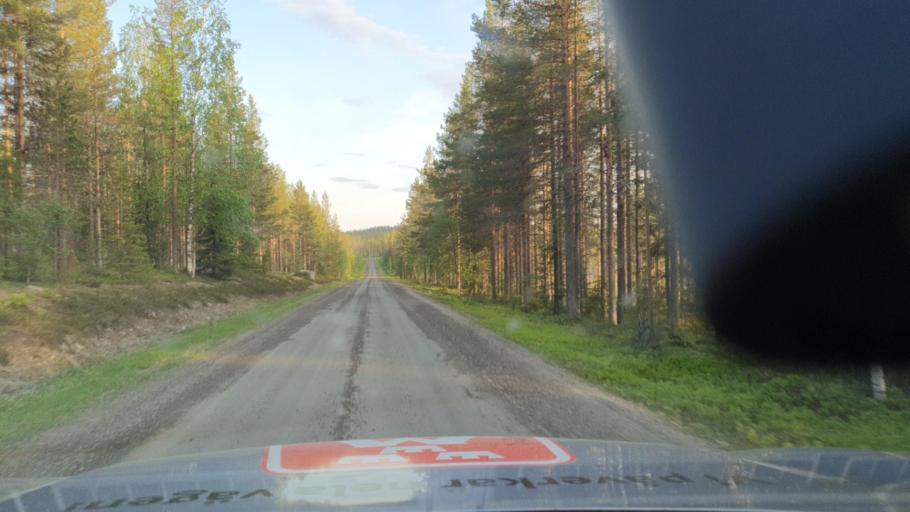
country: SE
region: Norrbotten
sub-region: Bodens Kommun
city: Boden
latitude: 66.4264
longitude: 21.7150
